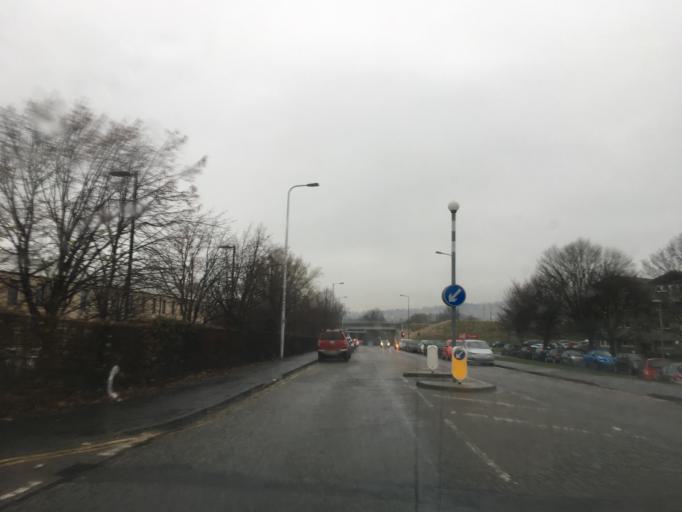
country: GB
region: Scotland
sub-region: Edinburgh
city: Colinton
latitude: 55.9307
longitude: -3.2733
